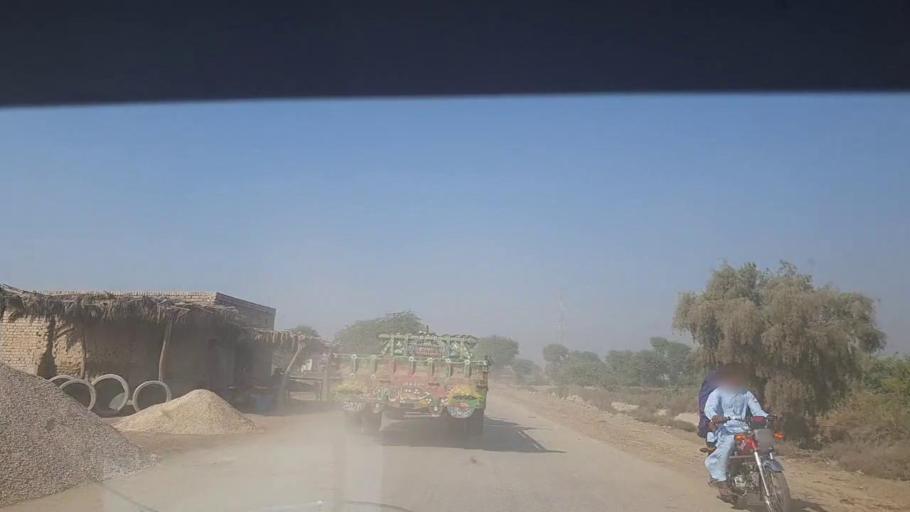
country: PK
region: Sindh
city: Kot Diji
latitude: 27.4377
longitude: 68.6346
